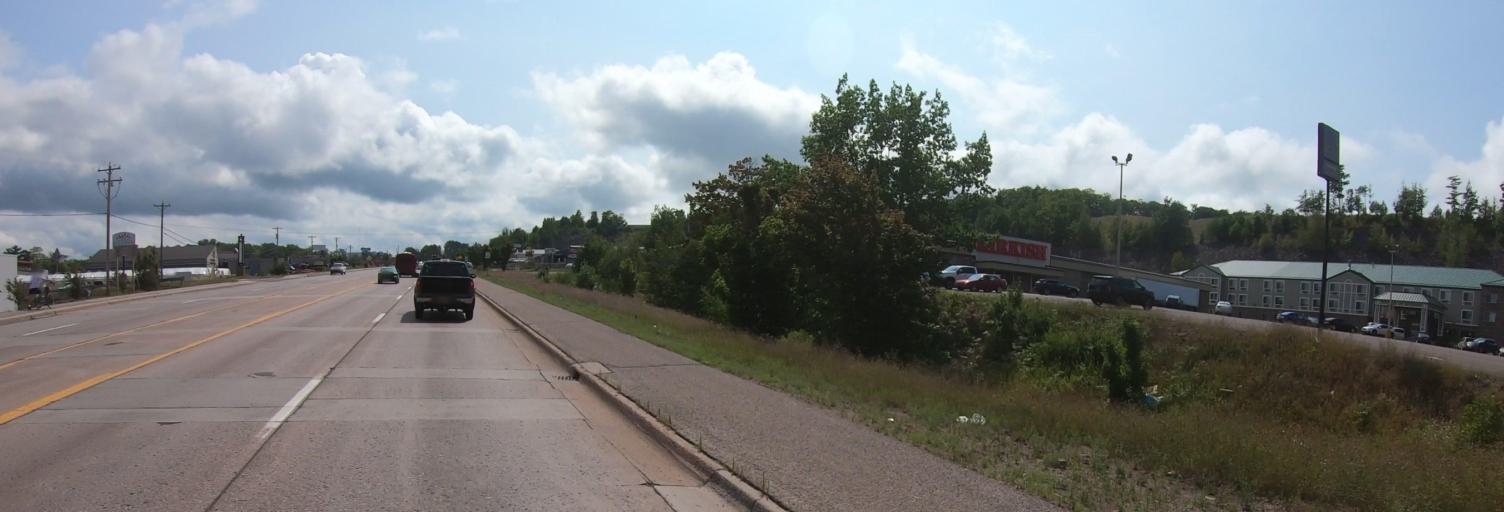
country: US
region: Michigan
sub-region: Houghton County
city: Hancock
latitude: 47.1124
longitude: -88.5891
